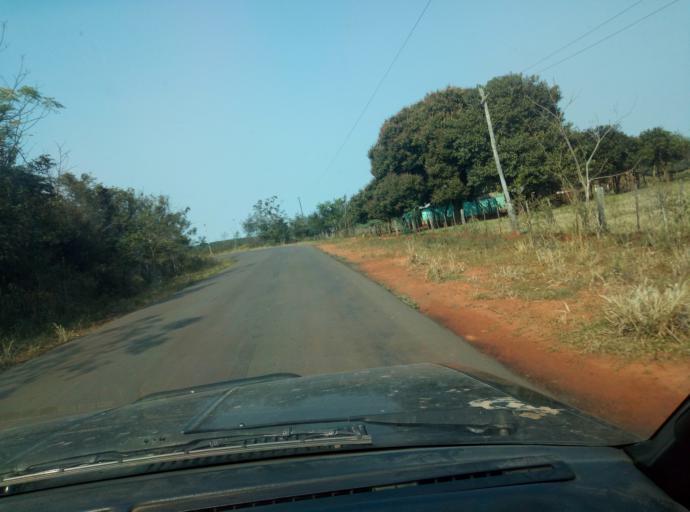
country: PY
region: Caaguazu
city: Carayao
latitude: -25.2343
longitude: -56.2889
